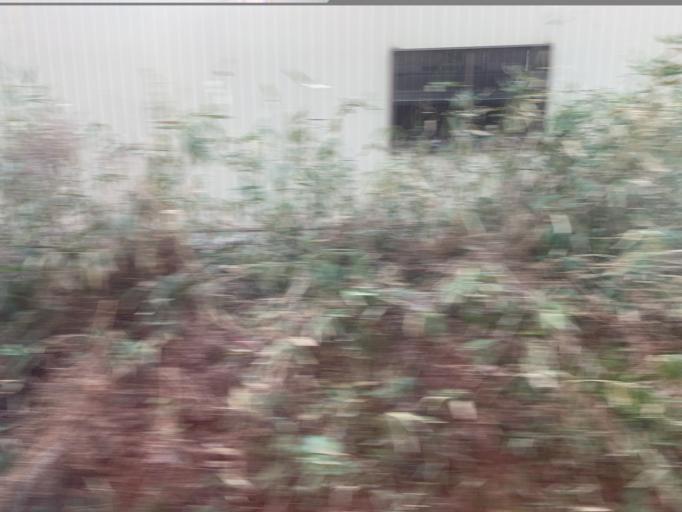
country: JP
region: Gifu
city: Takayama
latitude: 35.9274
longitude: 137.2117
